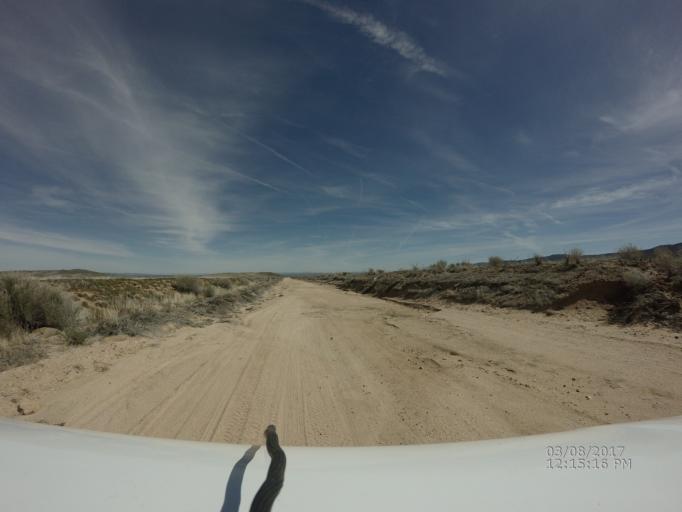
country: US
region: California
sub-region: Los Angeles County
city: Green Valley
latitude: 34.7171
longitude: -118.4184
